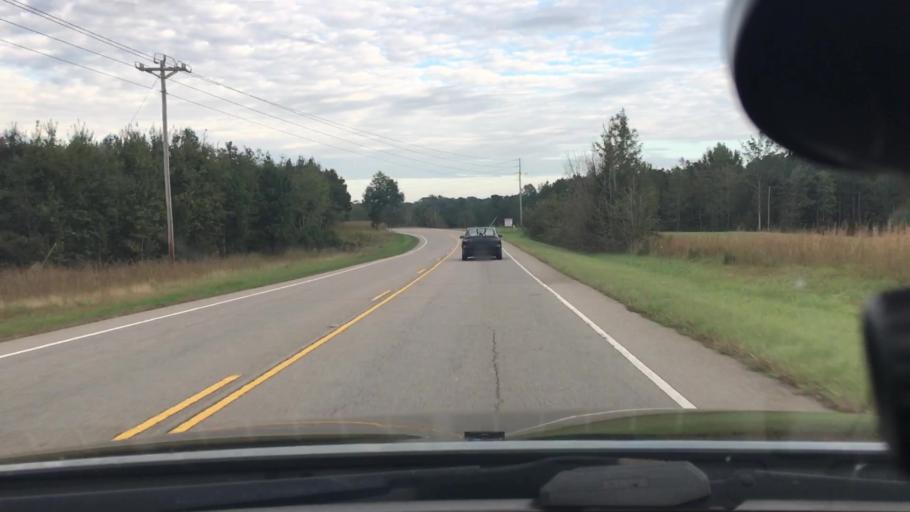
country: US
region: North Carolina
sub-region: Moore County
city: Robbins
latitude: 35.3992
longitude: -79.5492
